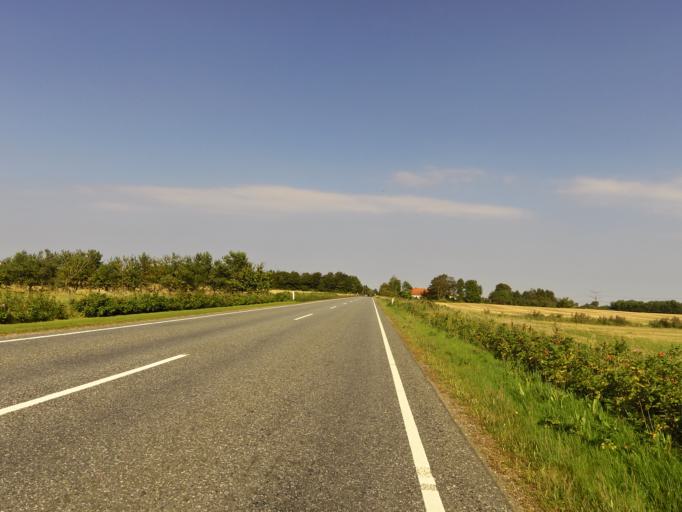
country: DK
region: South Denmark
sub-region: Vejen Kommune
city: Vejen
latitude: 55.4075
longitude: 9.1519
